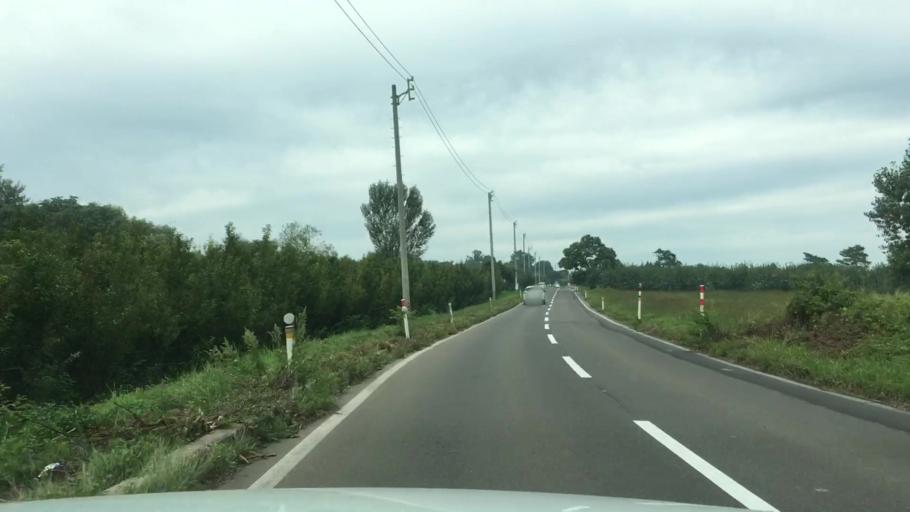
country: JP
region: Aomori
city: Hirosaki
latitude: 40.6692
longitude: 140.3893
